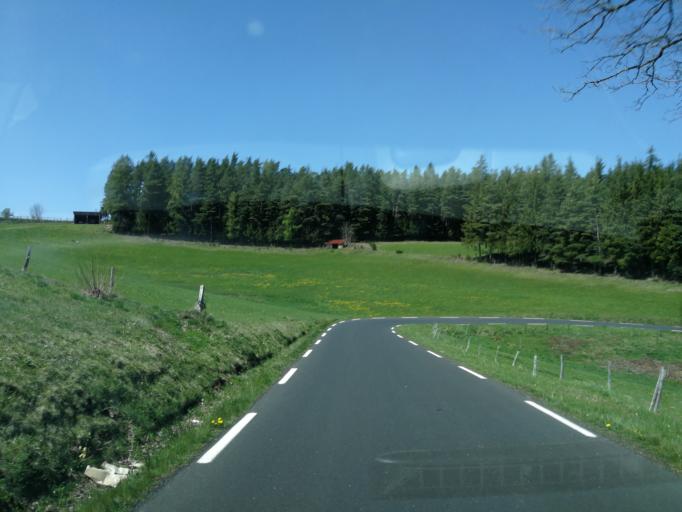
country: FR
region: Auvergne
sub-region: Departement de la Haute-Loire
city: Dunieres
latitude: 45.1993
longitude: 4.3437
